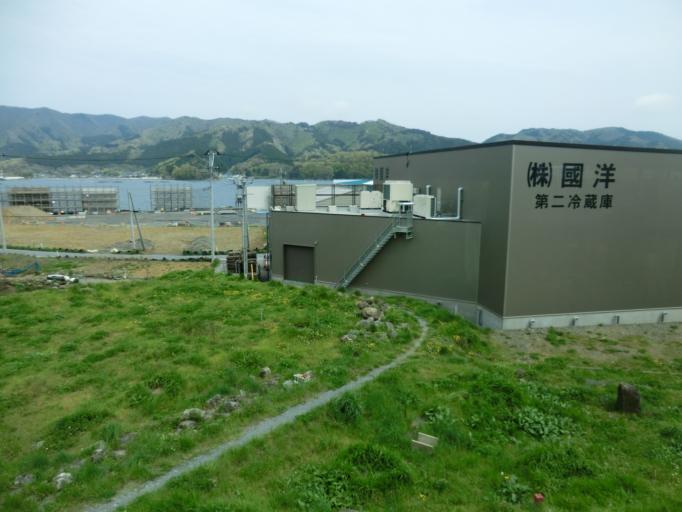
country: JP
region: Iwate
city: Ofunato
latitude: 39.0463
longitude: 141.7223
